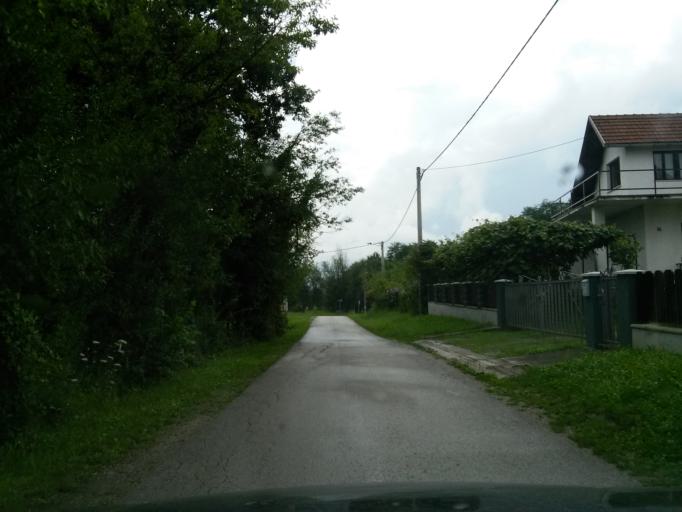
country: HR
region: Sisacko-Moslavacka
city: Glina
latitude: 45.2998
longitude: 15.9998
